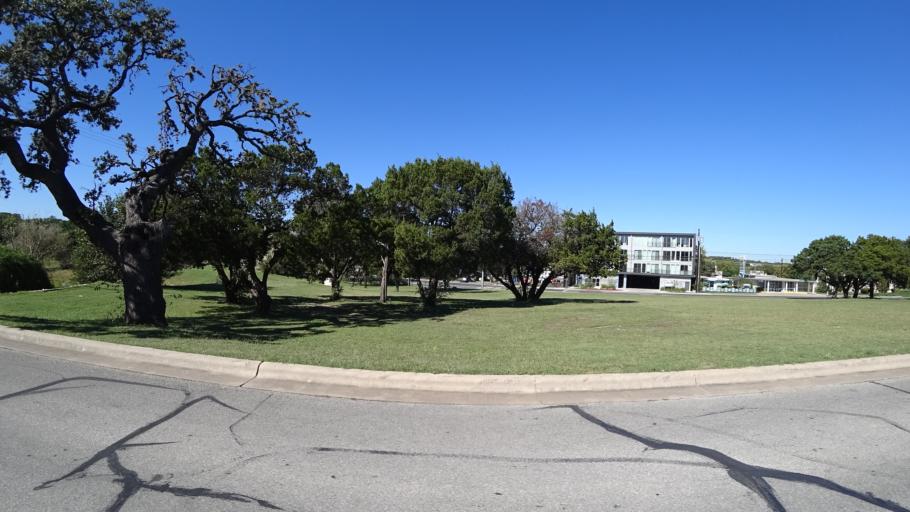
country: US
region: Texas
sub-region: Travis County
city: Austin
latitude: 30.2310
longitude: -97.7585
